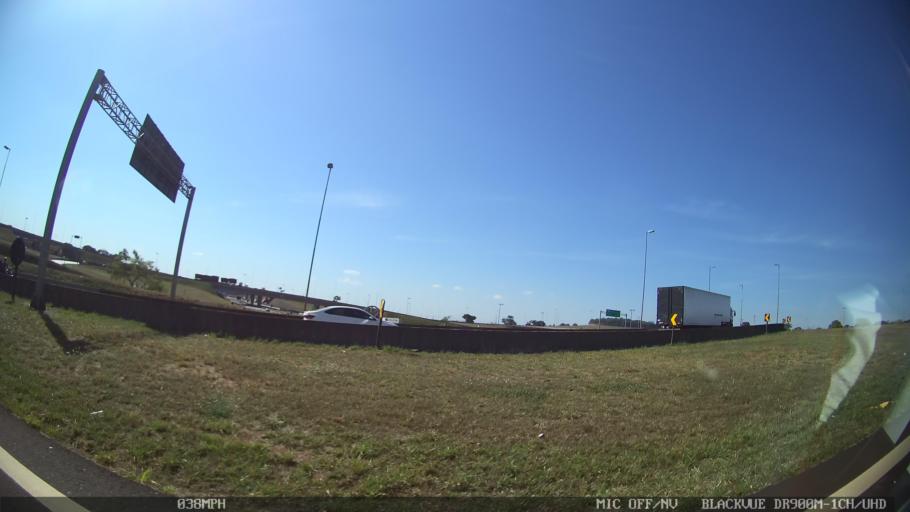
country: BR
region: Sao Paulo
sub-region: Ribeirao Preto
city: Ribeirao Preto
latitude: -21.2077
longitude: -47.7594
